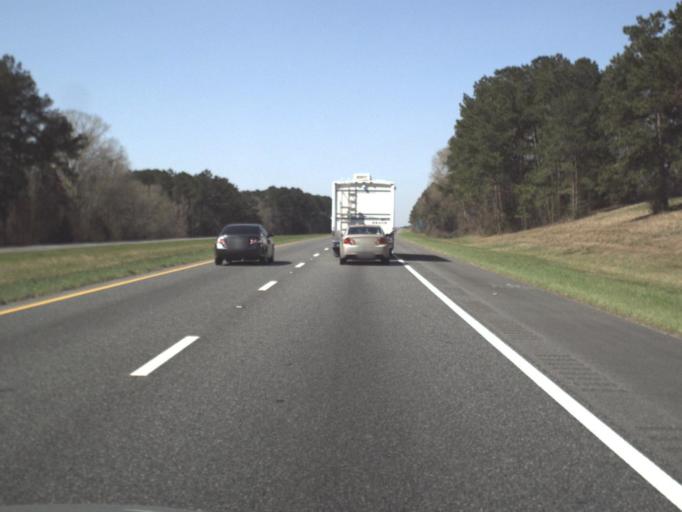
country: US
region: Florida
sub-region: Jackson County
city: Marianna
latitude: 30.7561
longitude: -85.3516
